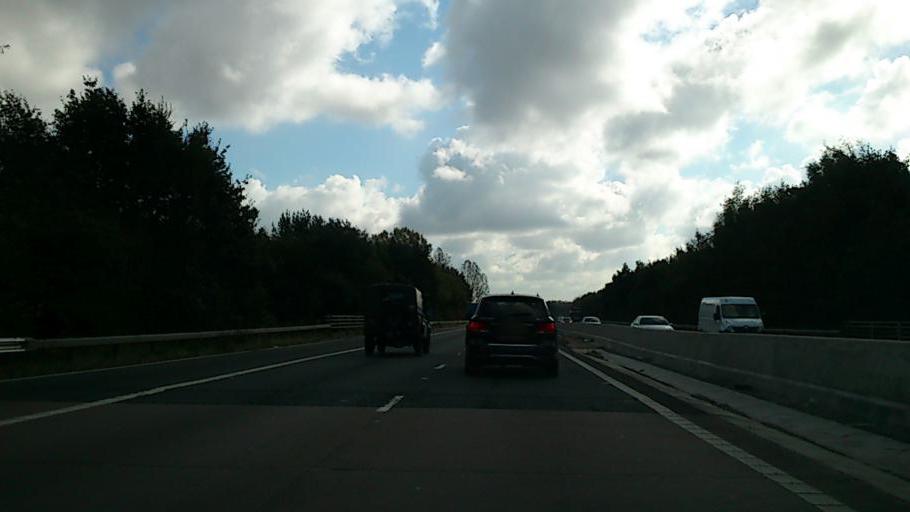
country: GB
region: England
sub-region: Shropshire
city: Tong
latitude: 52.6686
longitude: -2.3308
